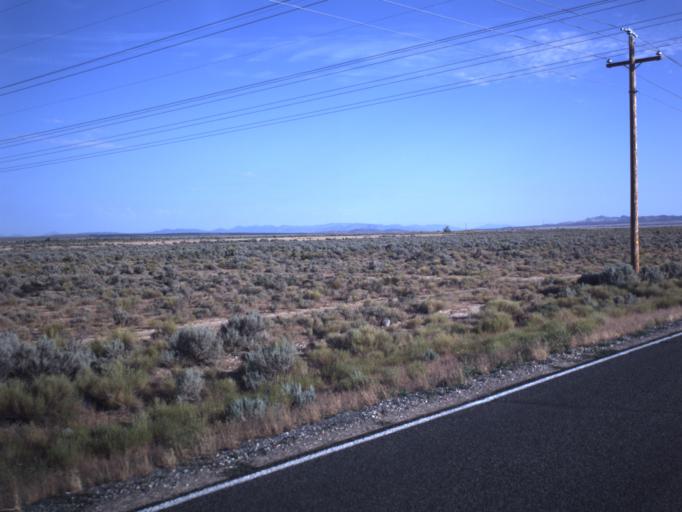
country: US
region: Utah
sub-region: Iron County
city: Enoch
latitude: 37.8018
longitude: -113.0506
